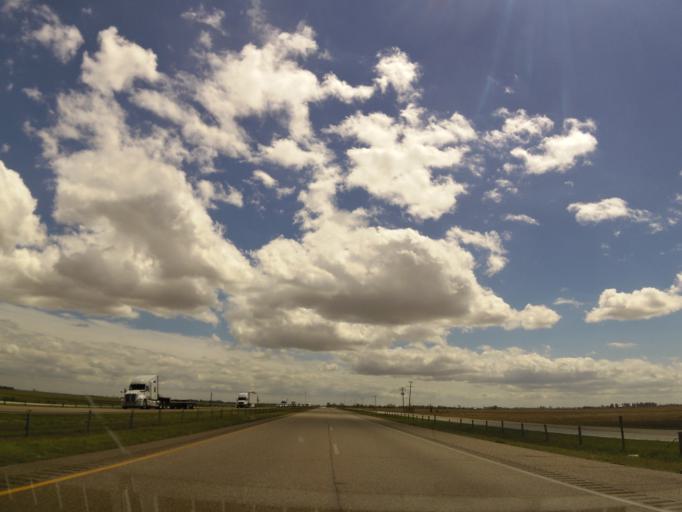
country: US
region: Arkansas
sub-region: Crittenden County
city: Marion
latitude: 35.3379
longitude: -90.2681
